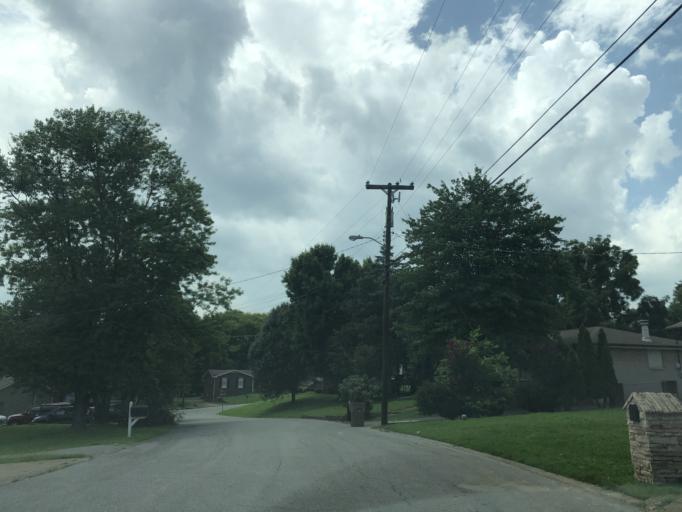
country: US
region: Tennessee
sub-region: Williamson County
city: Brentwood Estates
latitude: 36.0588
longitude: -86.6926
